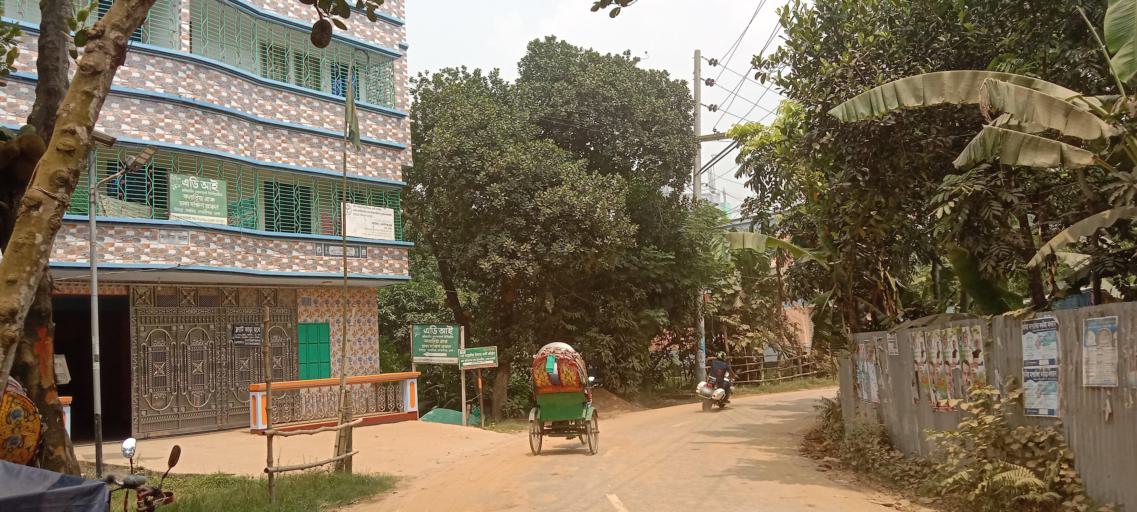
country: BD
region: Dhaka
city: Azimpur
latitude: 23.7242
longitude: 90.2743
